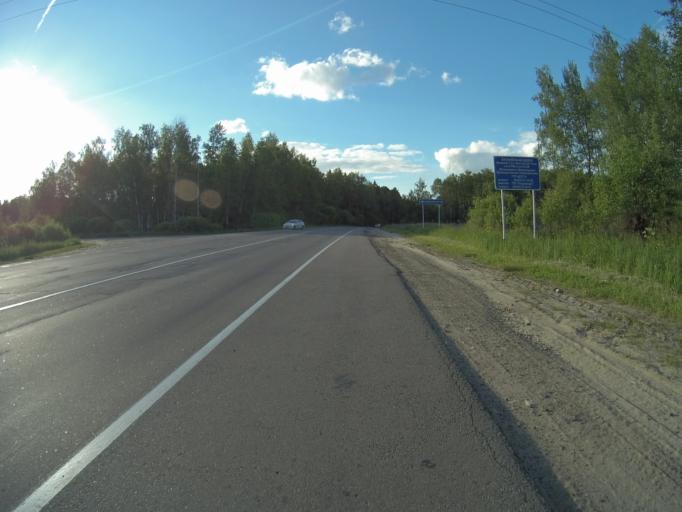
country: RU
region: Vladimir
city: Anopino
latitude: 55.8407
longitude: 40.6418
